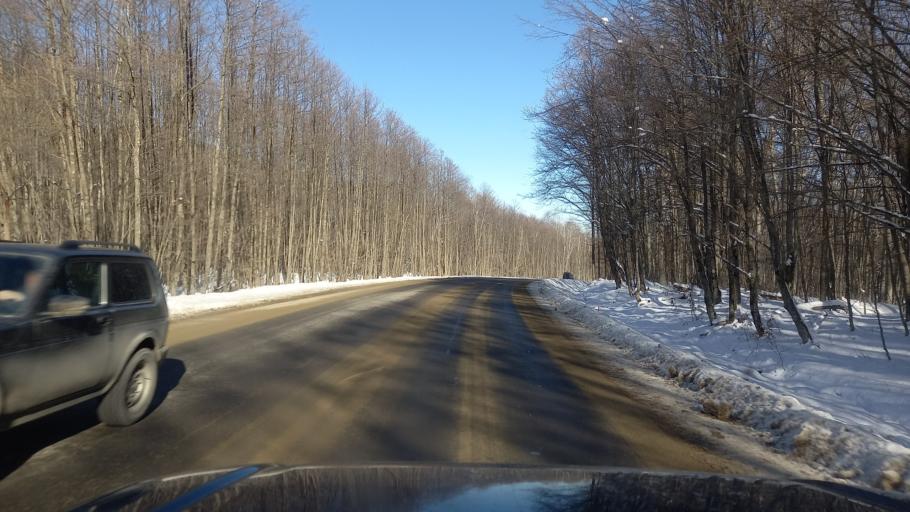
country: RU
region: Adygeya
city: Kamennomostskiy
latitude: 44.2155
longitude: 40.0771
